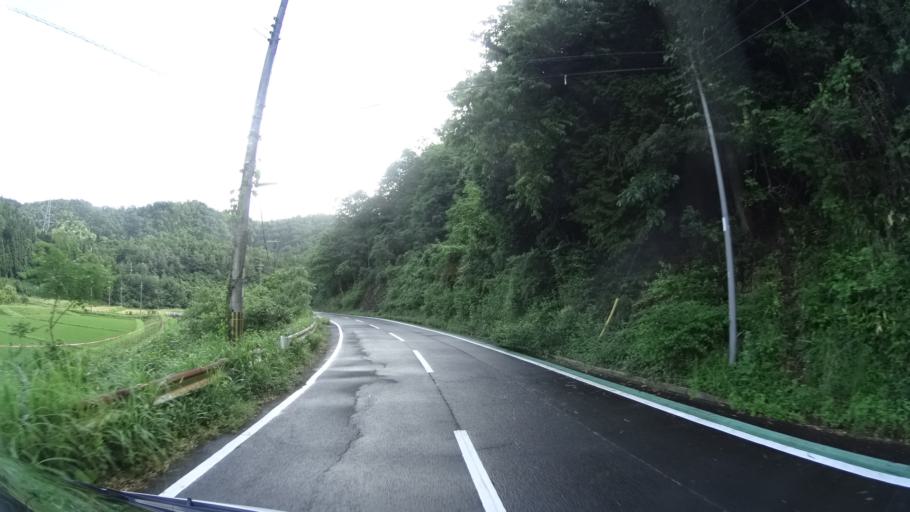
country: JP
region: Kyoto
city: Ayabe
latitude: 35.3835
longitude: 135.2564
